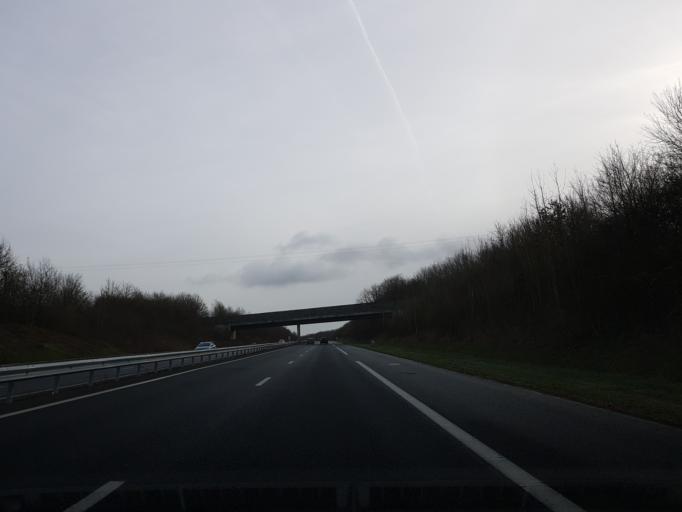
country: FR
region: Bourgogne
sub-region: Departement de l'Yonne
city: Soucy
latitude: 48.2393
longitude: 3.3705
